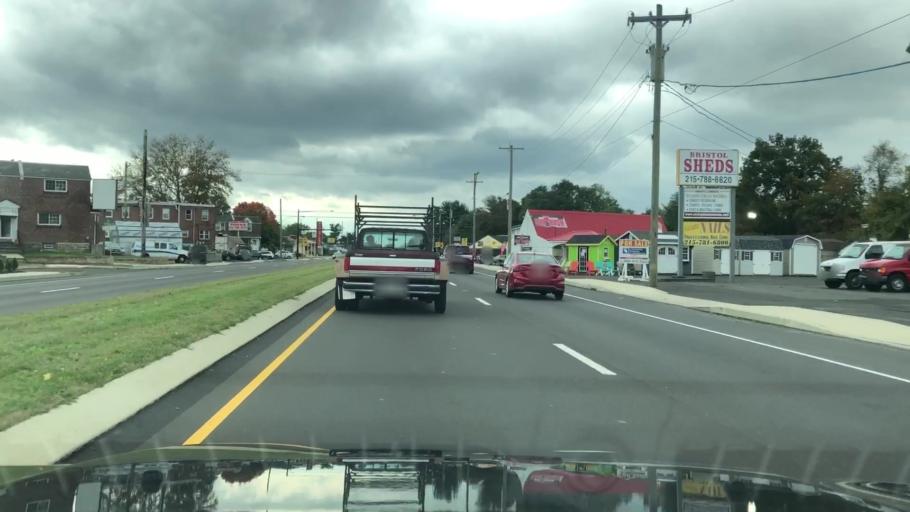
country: US
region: Pennsylvania
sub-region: Bucks County
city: Bristol
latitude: 40.1079
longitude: -74.8576
